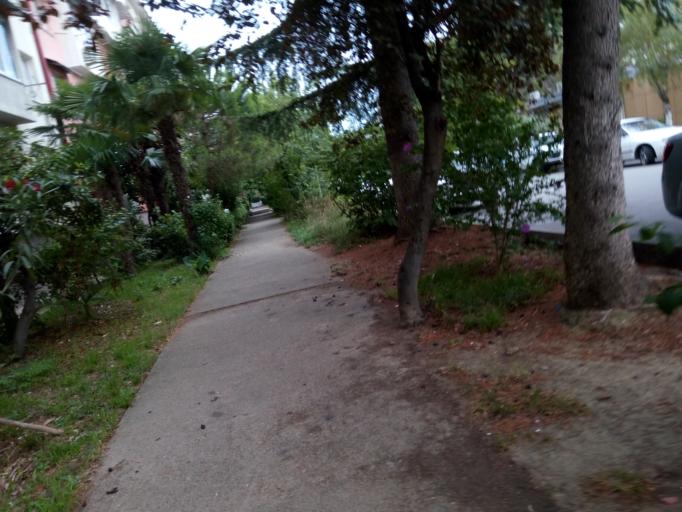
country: RU
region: Krasnodarskiy
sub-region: Sochi City
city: Sochi
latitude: 43.5663
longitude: 39.7605
